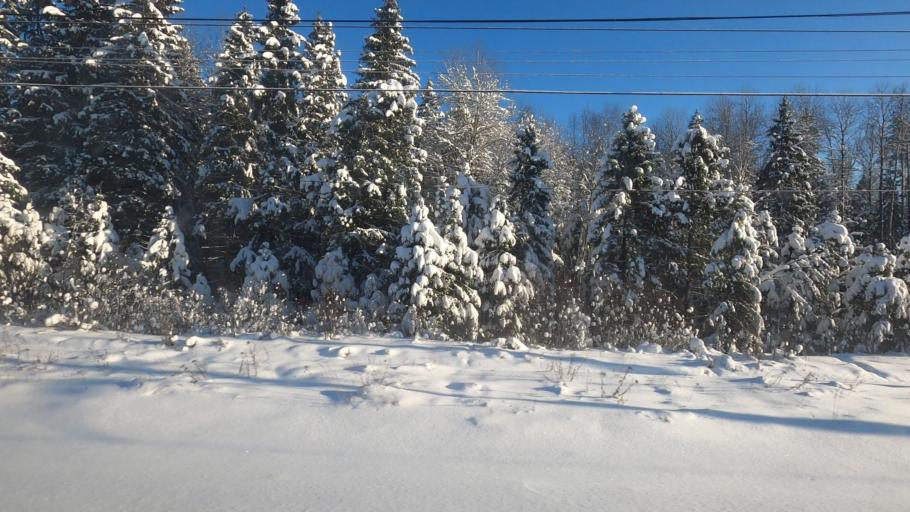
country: RU
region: Moskovskaya
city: Verbilki
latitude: 56.5335
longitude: 37.5602
